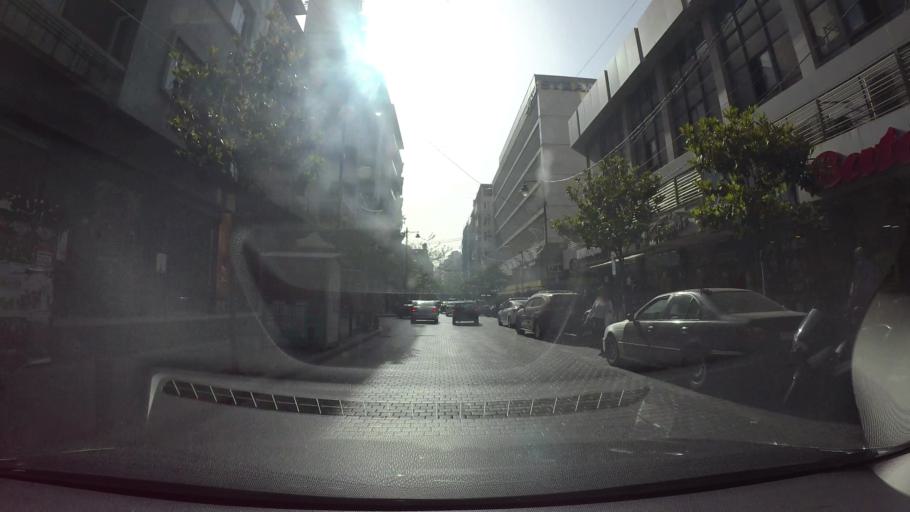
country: LB
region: Beyrouth
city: Ra's Bayrut
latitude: 33.8957
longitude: 35.4817
